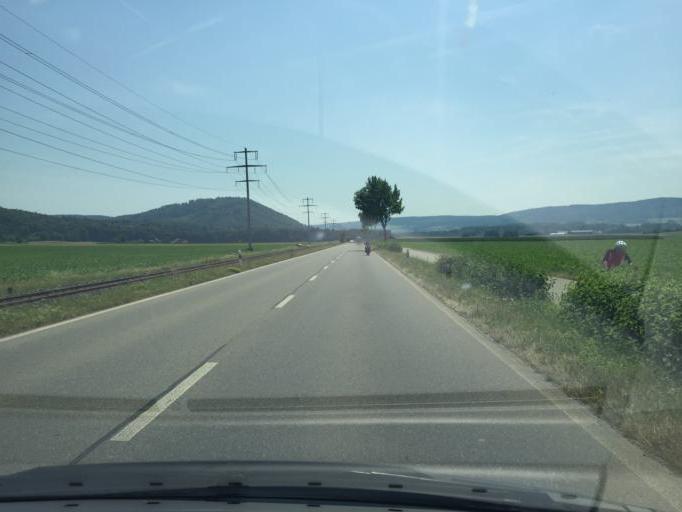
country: CH
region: Schaffhausen
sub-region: Bezirk Stein
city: Ramsen
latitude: 47.7005
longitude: 8.8226
